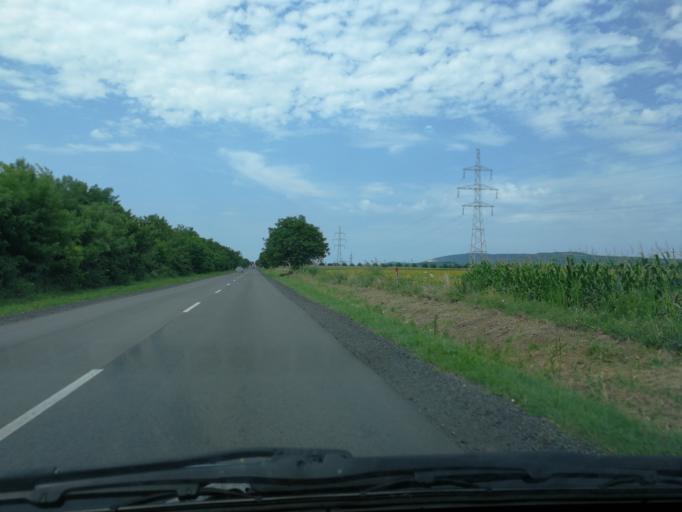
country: HU
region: Baranya
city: Siklos
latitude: 45.8488
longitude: 18.3689
